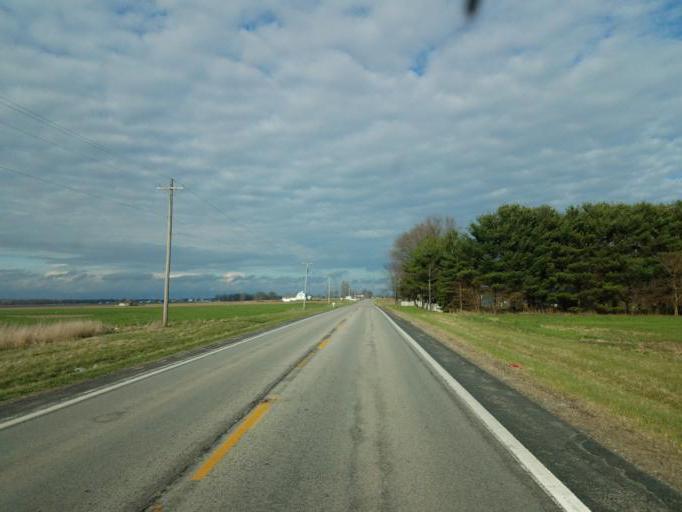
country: US
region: Ohio
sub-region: Delaware County
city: Delaware
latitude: 40.3203
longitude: -83.0247
